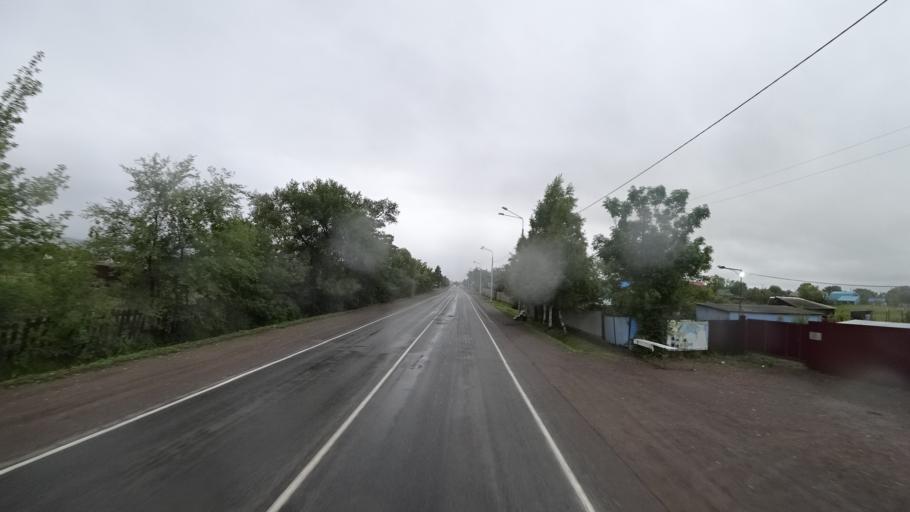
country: RU
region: Primorskiy
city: Chernigovka
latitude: 44.3340
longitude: 132.5802
